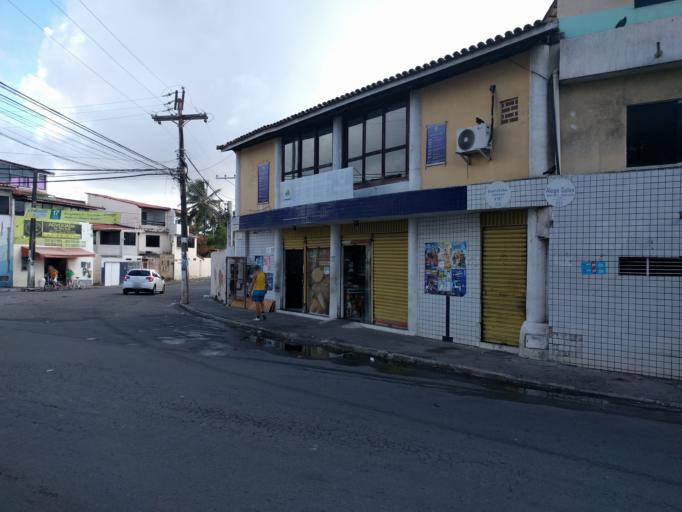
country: BR
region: Bahia
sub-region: Lauro De Freitas
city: Lauro de Freitas
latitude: -12.9388
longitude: -38.3398
